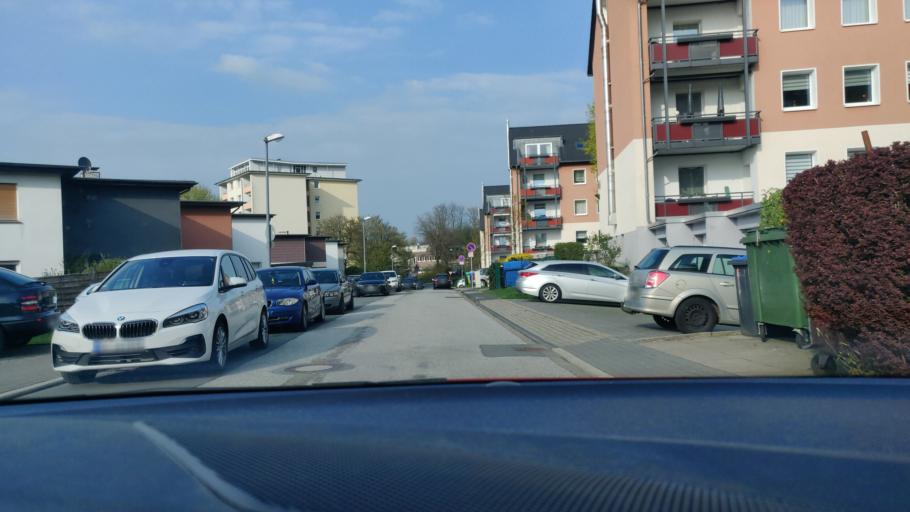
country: DE
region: North Rhine-Westphalia
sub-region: Regierungsbezirk Dusseldorf
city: Velbert
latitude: 51.3386
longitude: 7.0104
